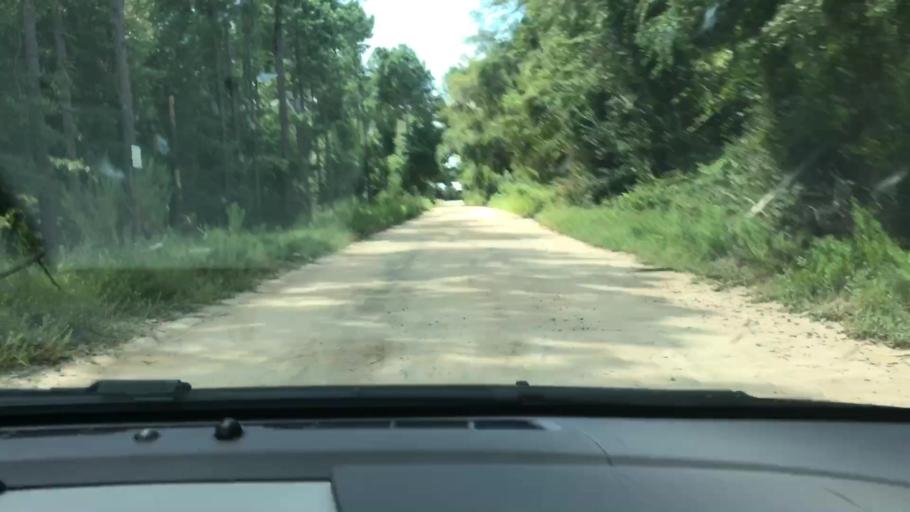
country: US
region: Georgia
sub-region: Clay County
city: Fort Gaines
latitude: 31.7335
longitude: -85.0906
